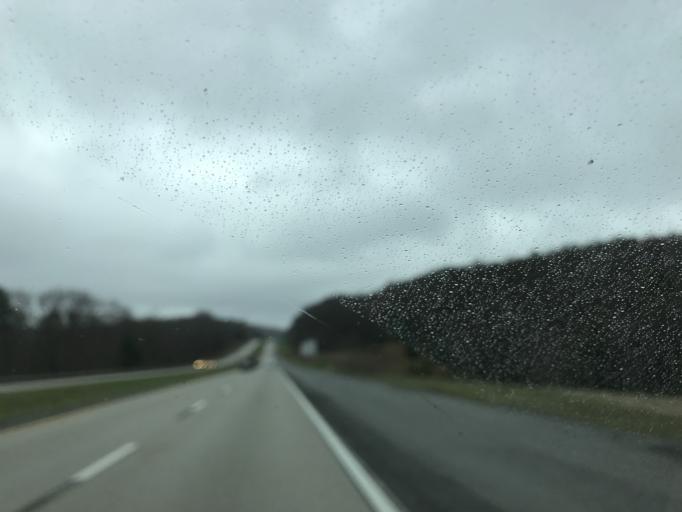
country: US
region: West Virginia
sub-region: Raleigh County
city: Shady Spring
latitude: 37.7661
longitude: -81.0186
